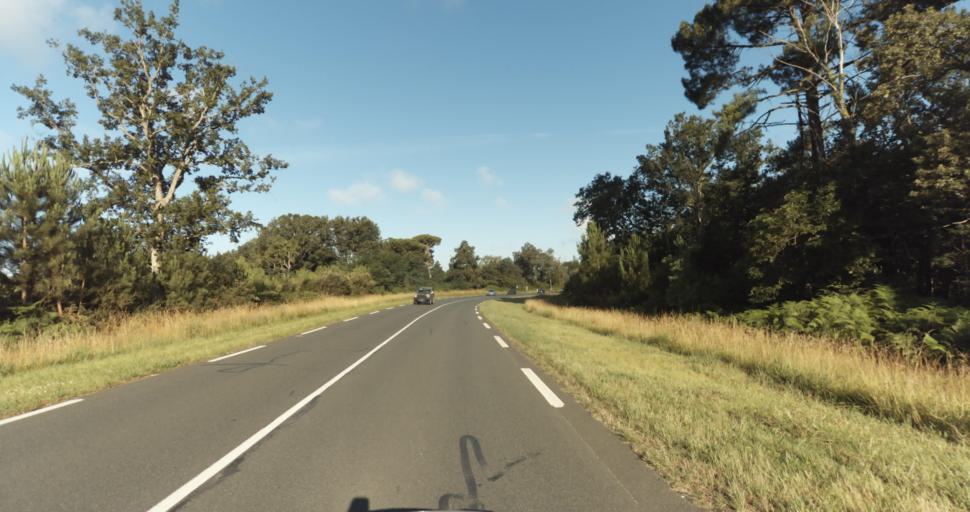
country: FR
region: Aquitaine
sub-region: Departement de la Gironde
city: Bazas
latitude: 44.4498
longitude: -0.2433
